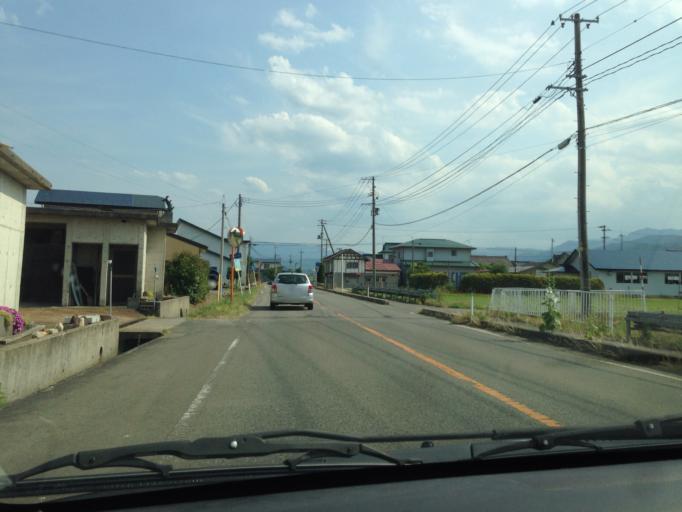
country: JP
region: Fukushima
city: Kitakata
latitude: 37.5069
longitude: 139.8328
